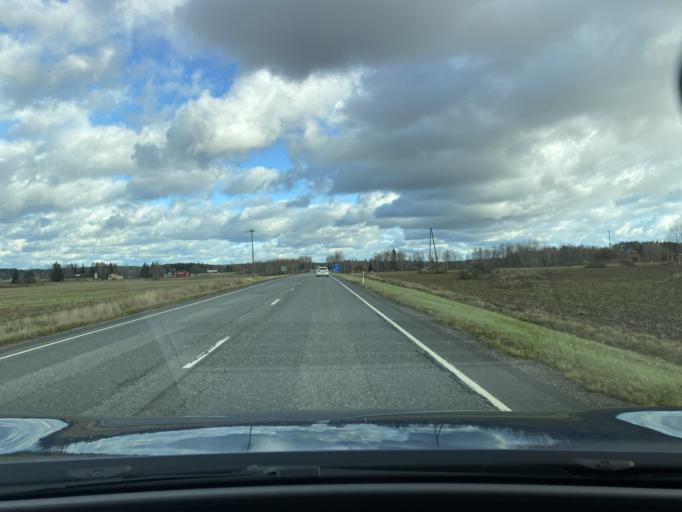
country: FI
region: Haeme
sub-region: Forssa
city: Humppila
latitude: 60.9506
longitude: 23.3270
